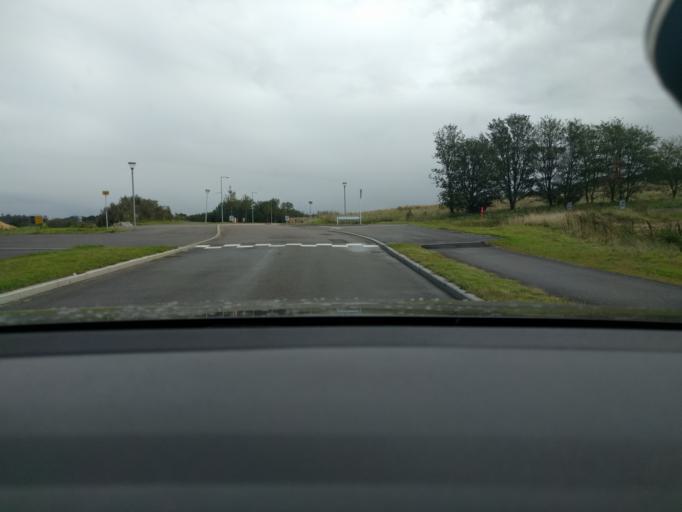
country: DK
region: Central Jutland
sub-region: Viborg Kommune
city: Viborg
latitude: 56.4229
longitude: 9.4071
